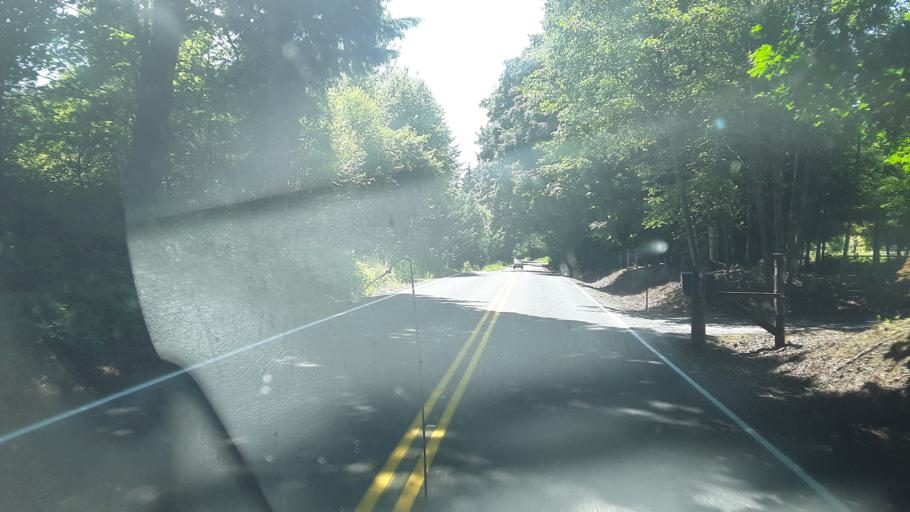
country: US
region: Washington
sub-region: Clark County
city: Amboy
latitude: 45.9235
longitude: -122.4286
